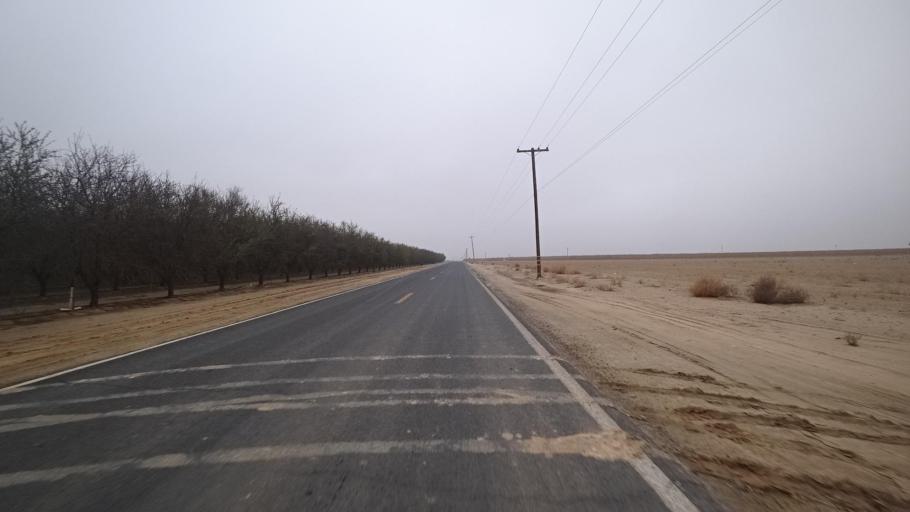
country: US
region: California
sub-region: Kern County
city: Lost Hills
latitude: 35.6114
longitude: -119.5803
